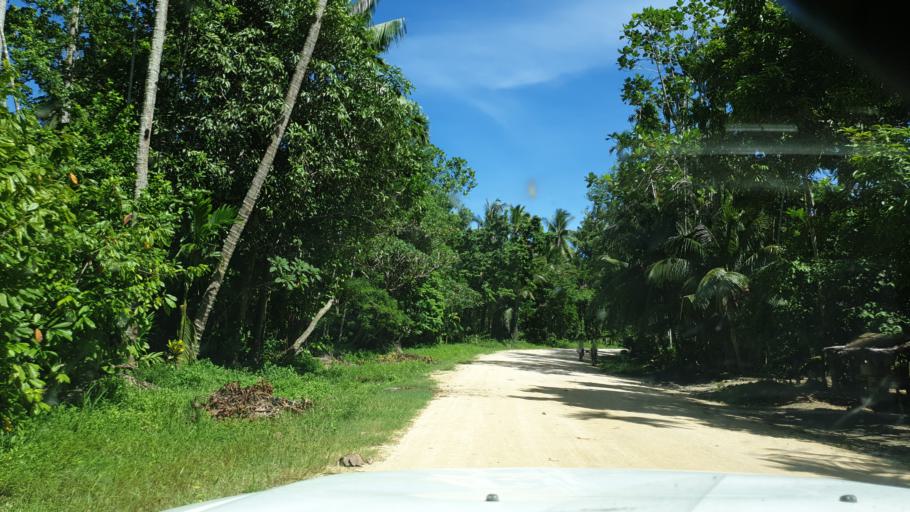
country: PG
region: Madang
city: Madang
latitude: -4.4981
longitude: 145.4171
